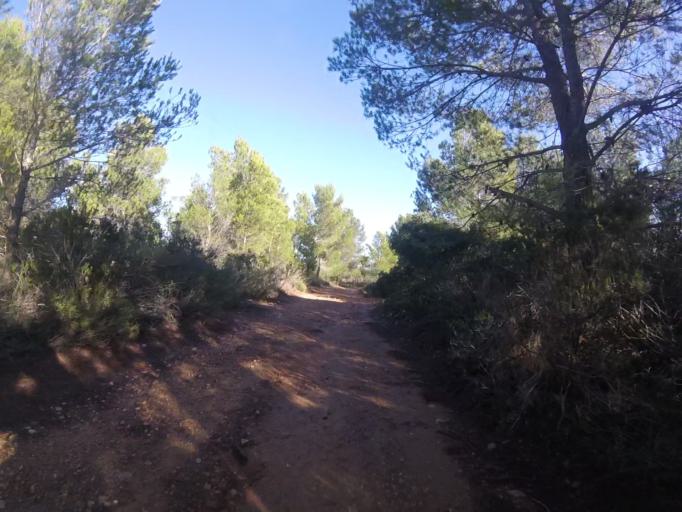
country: ES
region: Valencia
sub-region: Provincia de Castello
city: Sarratella
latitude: 40.2857
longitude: 0.0640
